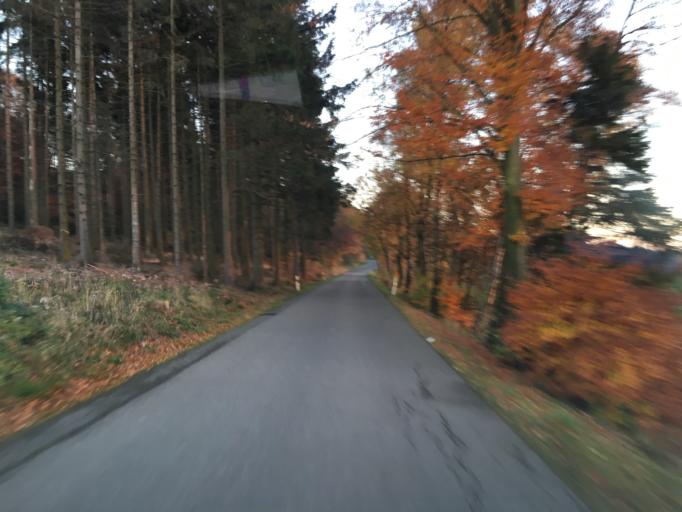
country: DE
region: North Rhine-Westphalia
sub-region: Regierungsbezirk Arnsberg
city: Luedenscheid
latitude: 51.2635
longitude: 7.6106
